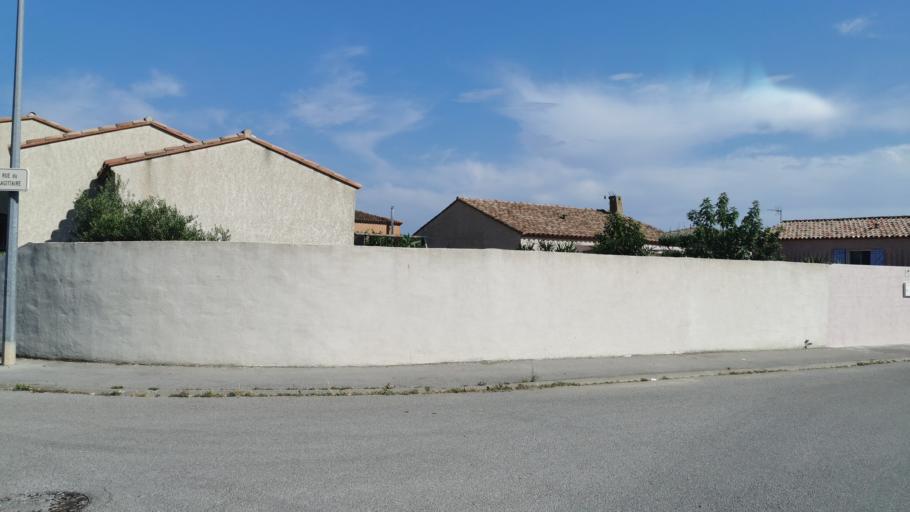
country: FR
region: Languedoc-Roussillon
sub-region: Departement de l'Aude
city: Narbonne
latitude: 43.1436
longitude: 2.9719
